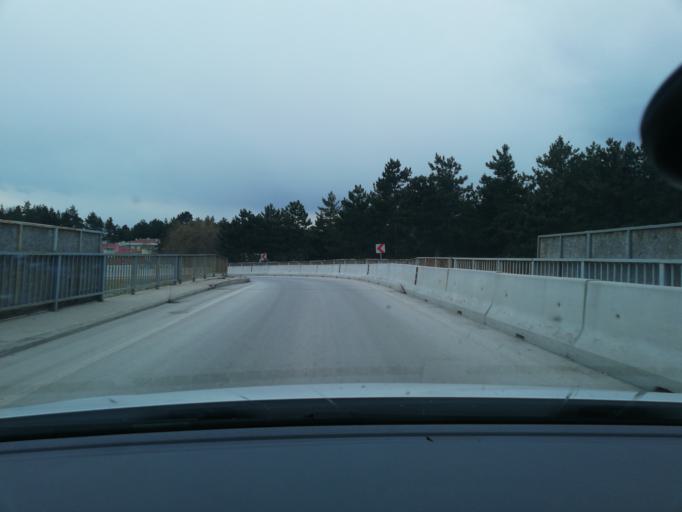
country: TR
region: Bolu
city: Gerede
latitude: 40.7946
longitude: 32.2052
